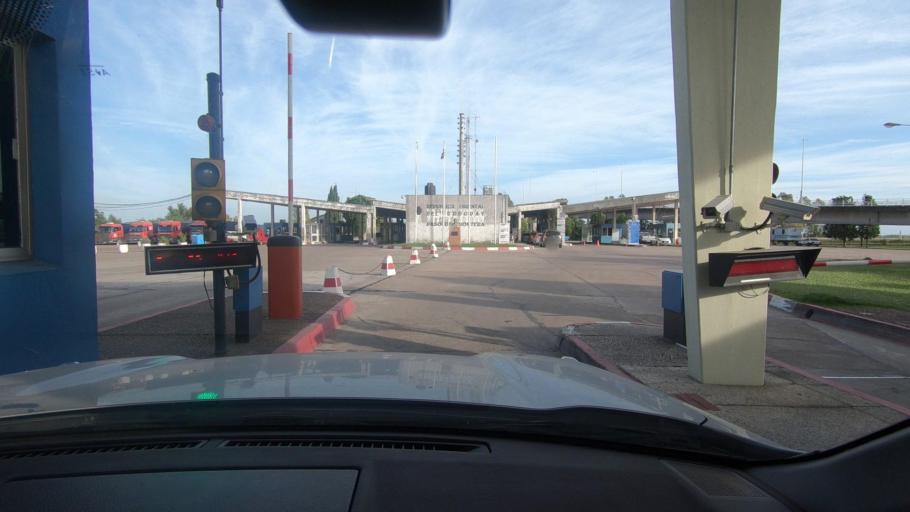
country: AR
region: Entre Rios
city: Colon
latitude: -32.2555
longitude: -58.1386
